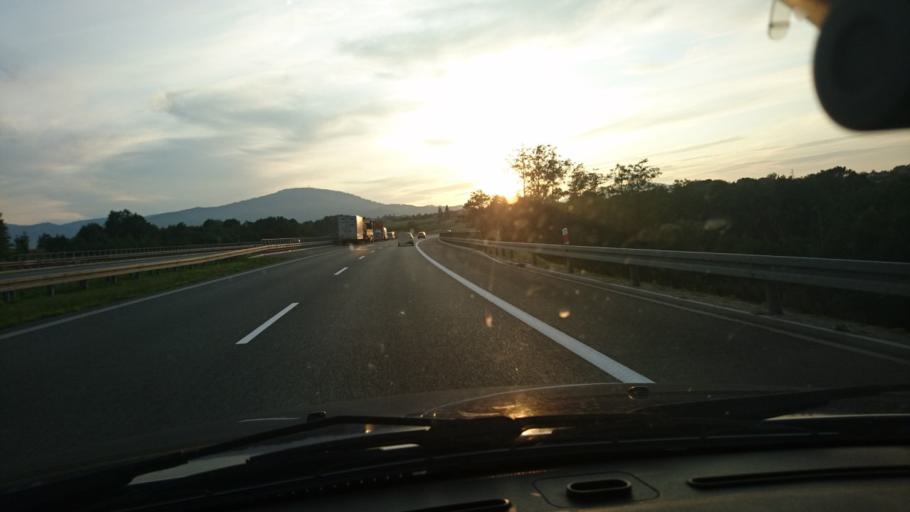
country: PL
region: Silesian Voivodeship
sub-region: Powiat zywiecki
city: Pietrzykowice
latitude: 49.6851
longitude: 19.1486
